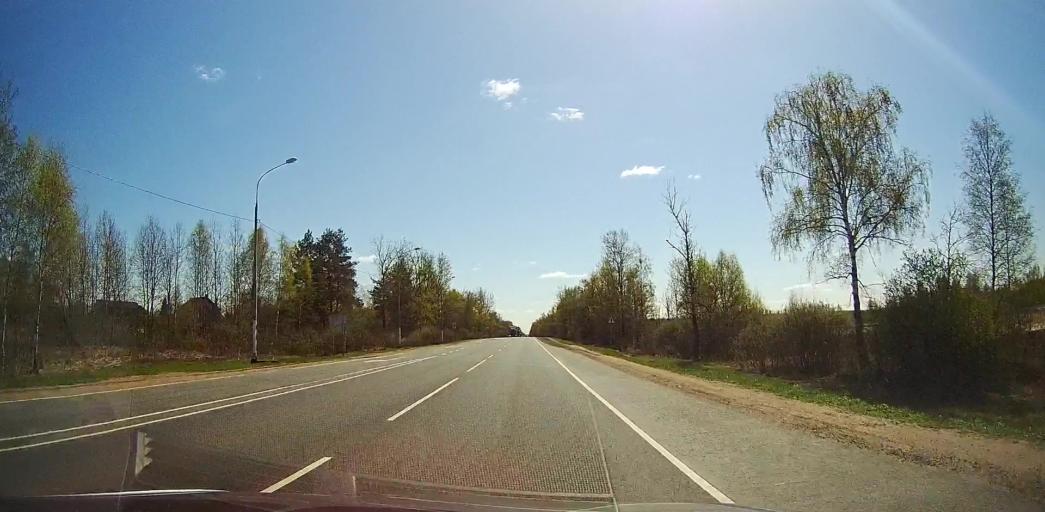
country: RU
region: Moskovskaya
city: Gzhel'
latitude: 55.5747
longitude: 38.3902
